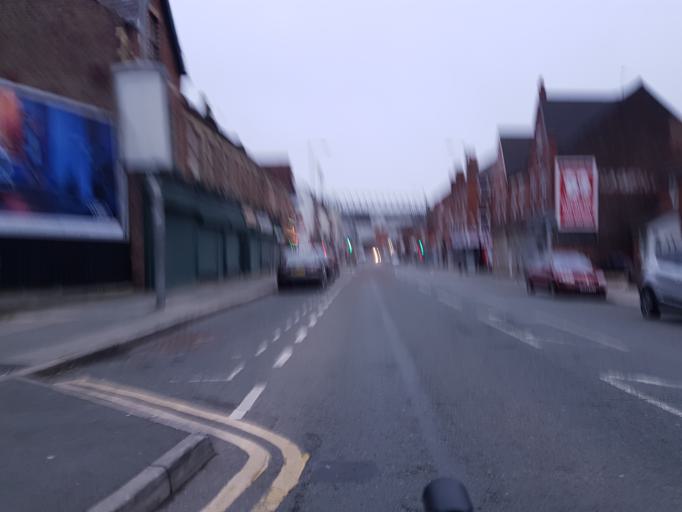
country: GB
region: England
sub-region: Liverpool
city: Liverpool
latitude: 53.4267
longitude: -2.9574
